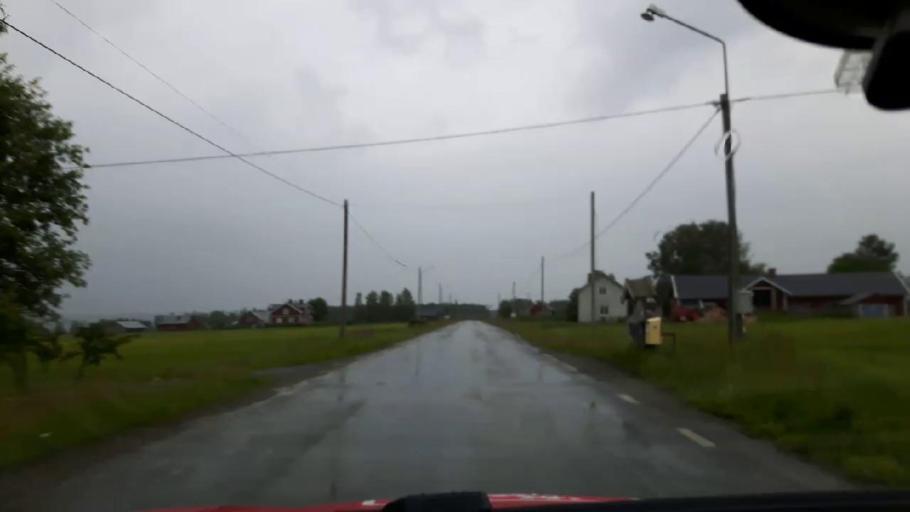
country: SE
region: Jaemtland
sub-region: OEstersunds Kommun
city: Brunflo
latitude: 62.9871
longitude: 14.8100
